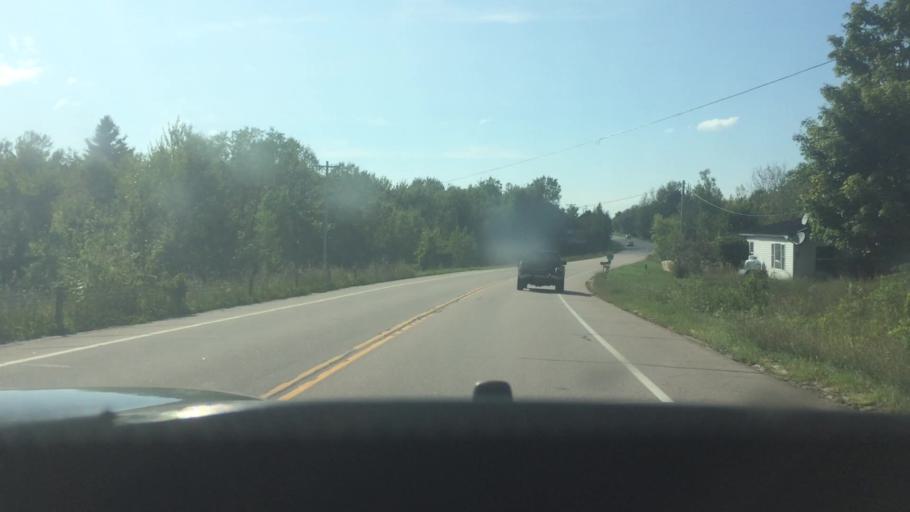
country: US
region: New York
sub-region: Franklin County
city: Malone
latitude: 44.8536
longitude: -74.2168
